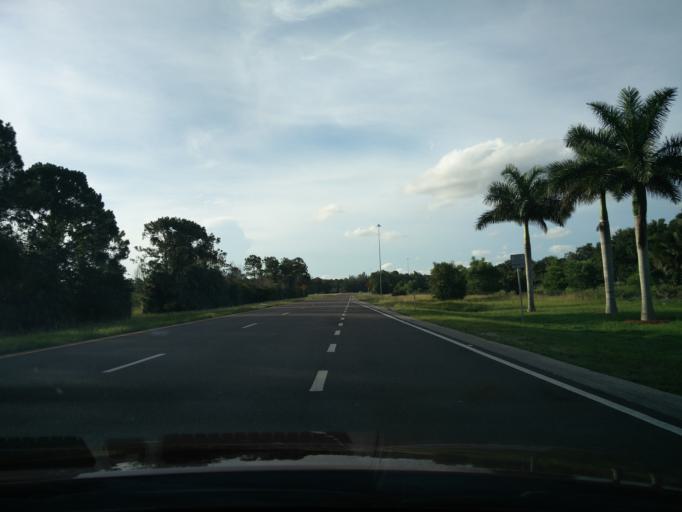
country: US
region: Florida
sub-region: Collier County
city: Vineyards
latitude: 26.2127
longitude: -81.7349
